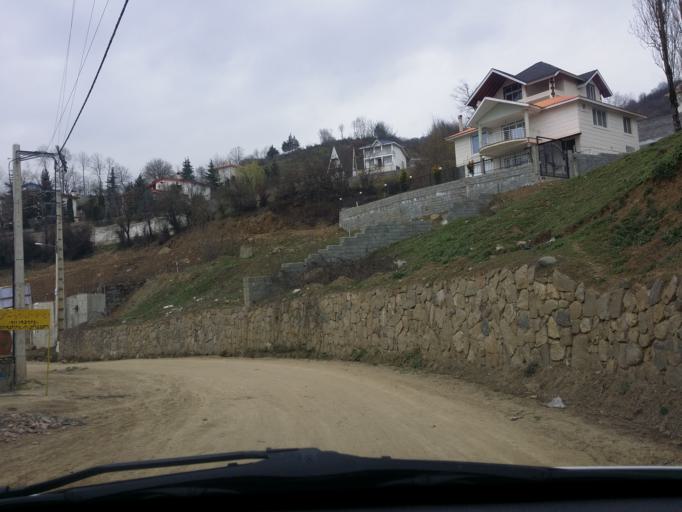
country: IR
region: Mazandaran
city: `Abbasabad
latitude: 36.5361
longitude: 51.1609
